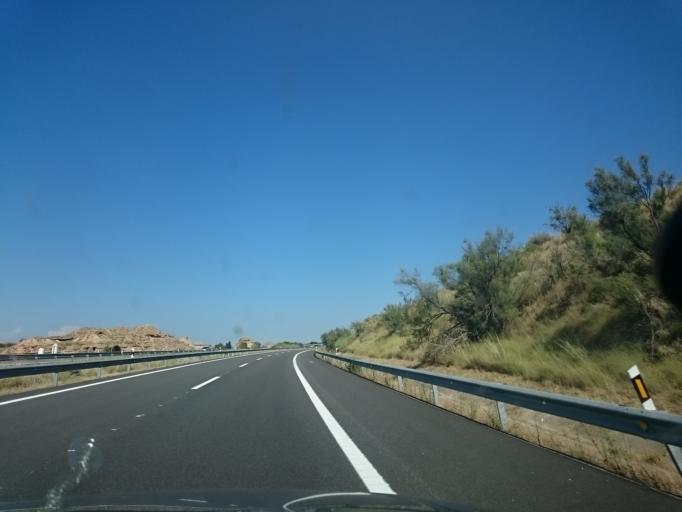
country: ES
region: Aragon
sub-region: Provincia de Huesca
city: Fraga
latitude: 41.4928
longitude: 0.3651
